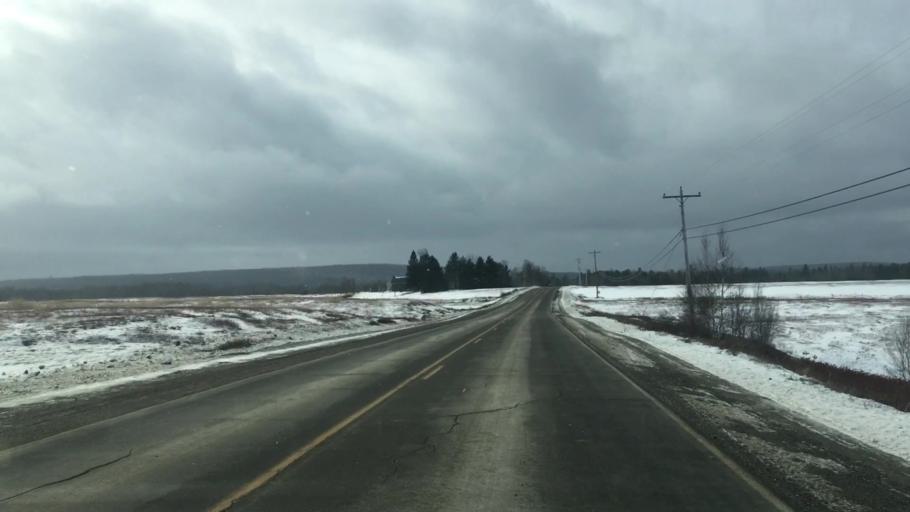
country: US
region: Maine
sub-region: Washington County
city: Calais
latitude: 45.0246
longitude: -67.3757
